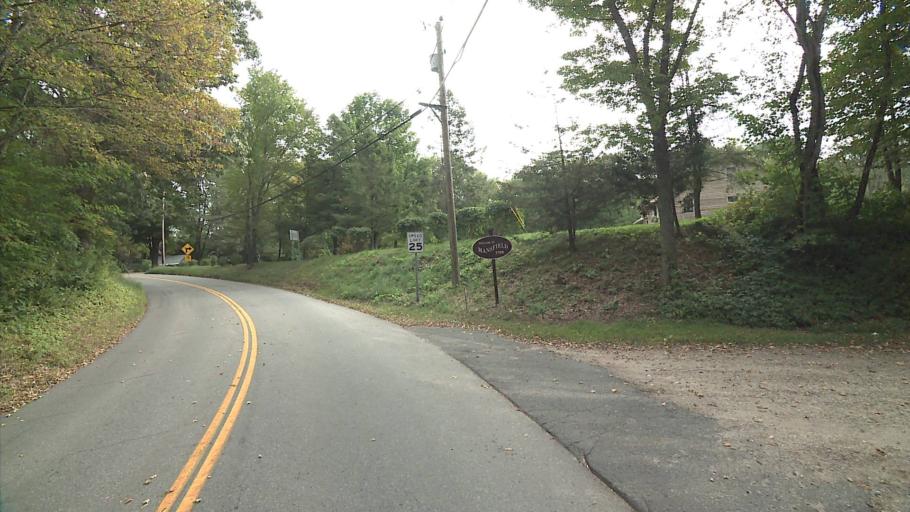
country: US
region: Connecticut
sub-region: Tolland County
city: South Coventry
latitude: 41.7847
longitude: -72.2791
